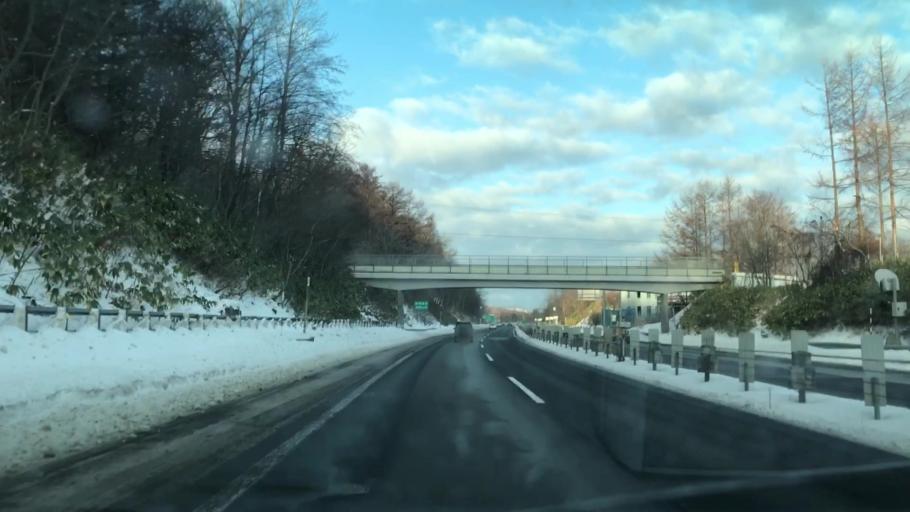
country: JP
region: Hokkaido
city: Otaru
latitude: 43.1370
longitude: 141.1590
